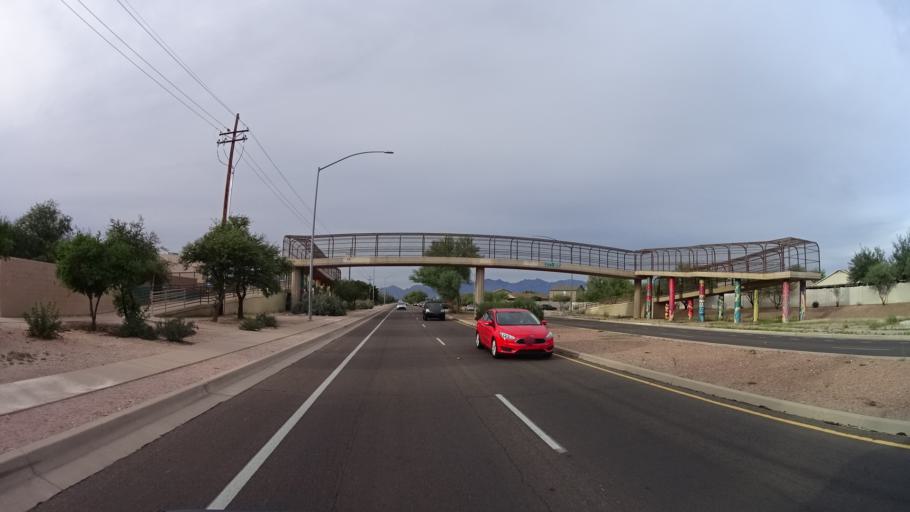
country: US
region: Arizona
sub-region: Pima County
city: South Tucson
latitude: 32.1551
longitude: -110.9351
